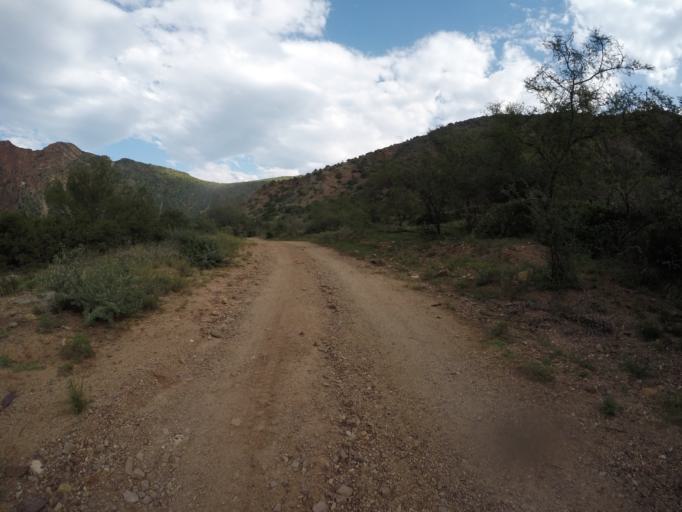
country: ZA
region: Eastern Cape
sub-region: Cacadu District Municipality
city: Kareedouw
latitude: -33.6372
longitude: 24.3166
